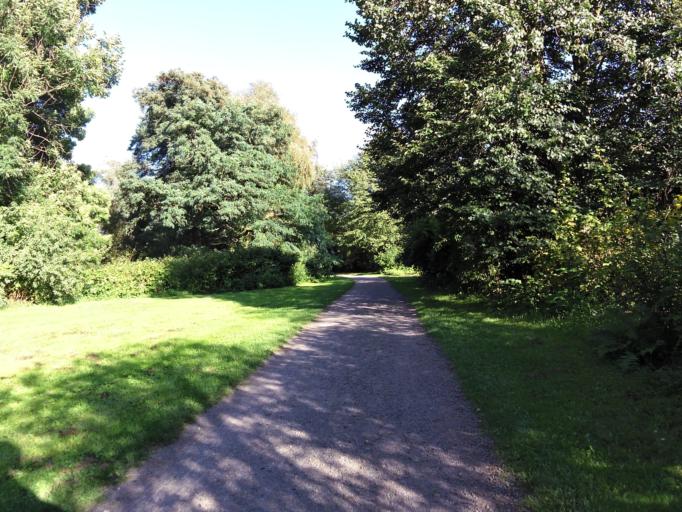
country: DE
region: Saxony
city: Markkleeberg
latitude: 51.2946
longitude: 12.3993
